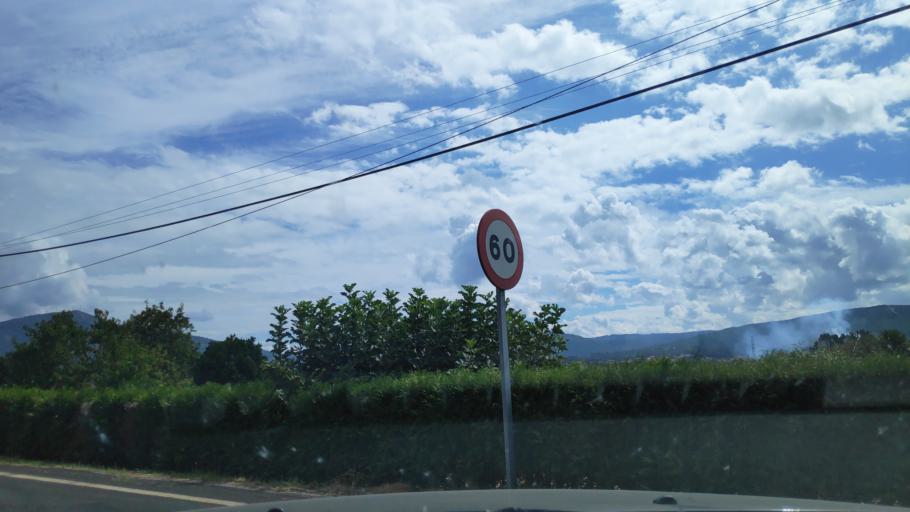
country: ES
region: Galicia
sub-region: Provincia da Coruna
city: Padron
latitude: 42.7276
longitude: -8.6743
